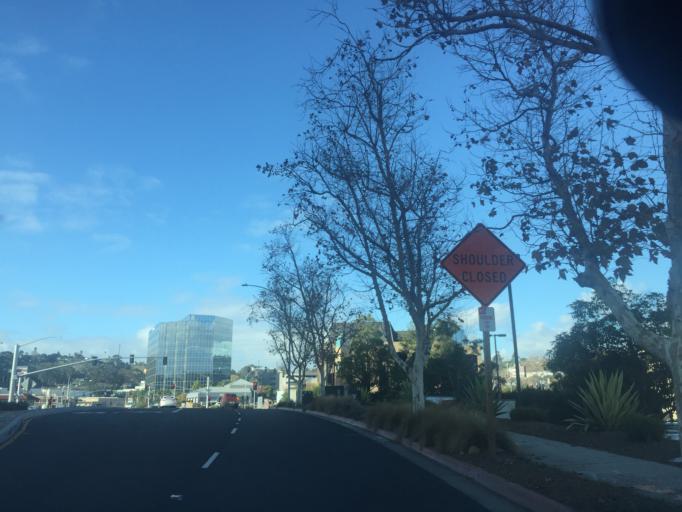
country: US
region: California
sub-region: San Diego County
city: San Diego
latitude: 32.7718
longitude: -117.1565
